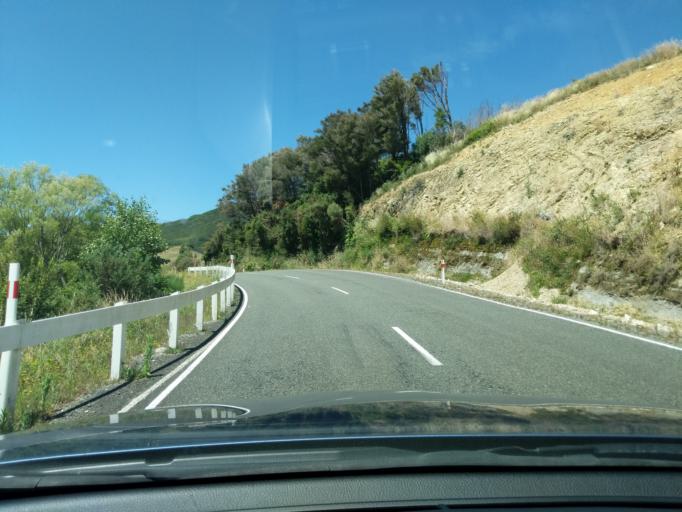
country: NZ
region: Tasman
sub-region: Tasman District
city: Takaka
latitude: -40.7414
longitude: 172.5715
